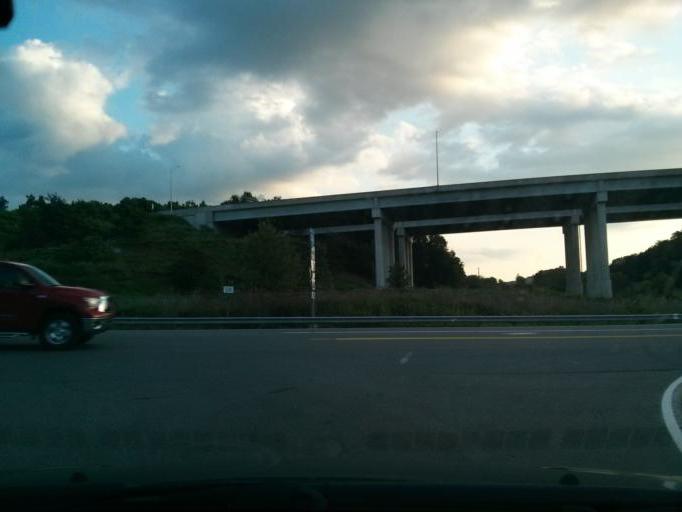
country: US
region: Pennsylvania
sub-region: Centre County
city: Park Forest Village
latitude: 40.8229
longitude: -77.9434
